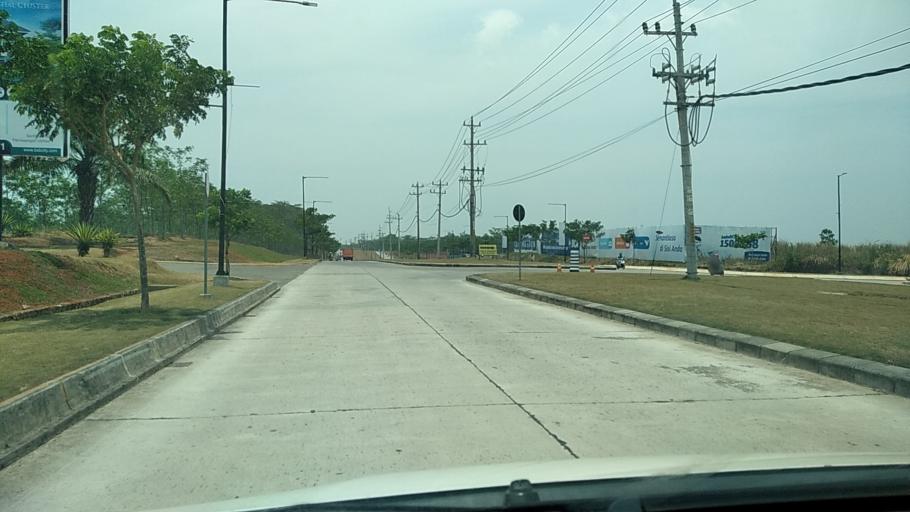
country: ID
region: Central Java
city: Semarang
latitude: -7.0402
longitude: 110.3303
